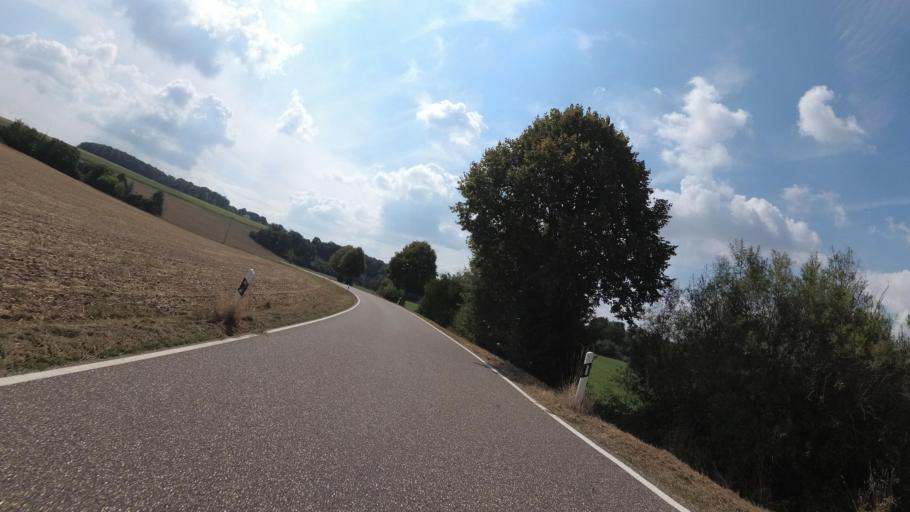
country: DE
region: Rheinland-Pfalz
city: Dietrichingen
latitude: 49.1993
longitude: 7.4148
